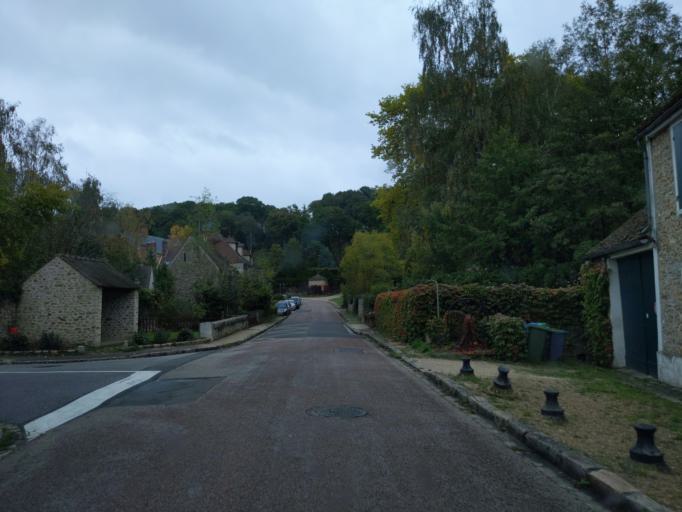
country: FR
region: Ile-de-France
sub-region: Departement des Yvelines
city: Bullion
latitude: 48.6361
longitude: 1.9540
